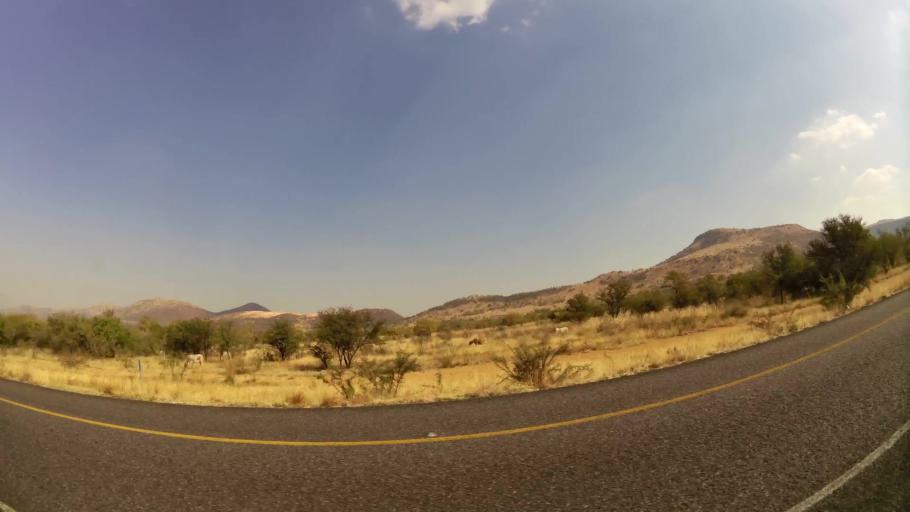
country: ZA
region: North-West
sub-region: Bojanala Platinum District Municipality
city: Rustenburg
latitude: -25.6073
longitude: 27.1439
